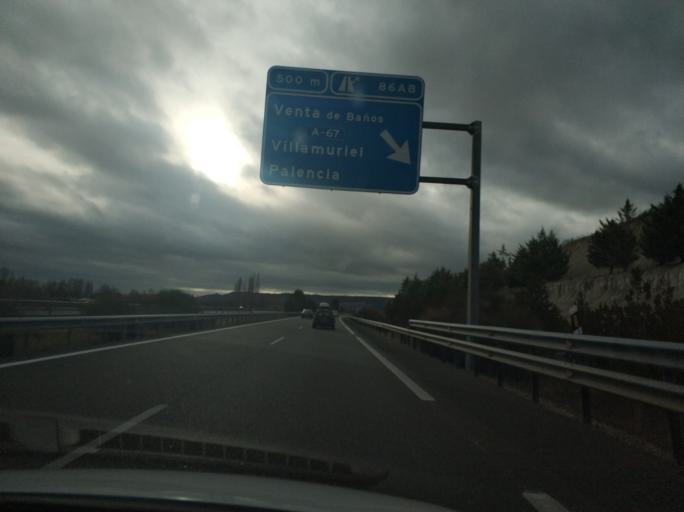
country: ES
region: Castille and Leon
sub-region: Provincia de Palencia
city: Venta de Banos
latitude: 41.9408
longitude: -4.4872
